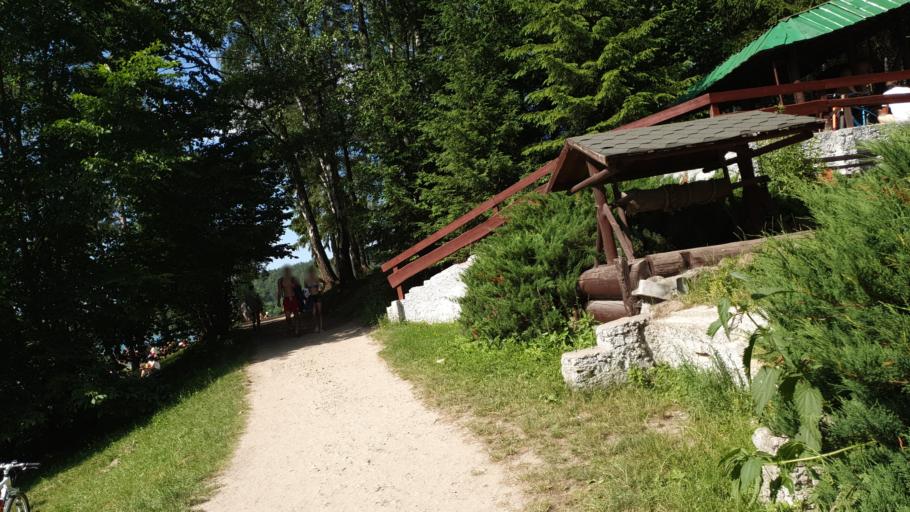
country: LT
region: Vilnius County
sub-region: Vilnius
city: Fabijoniskes
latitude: 54.7847
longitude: 25.3336
